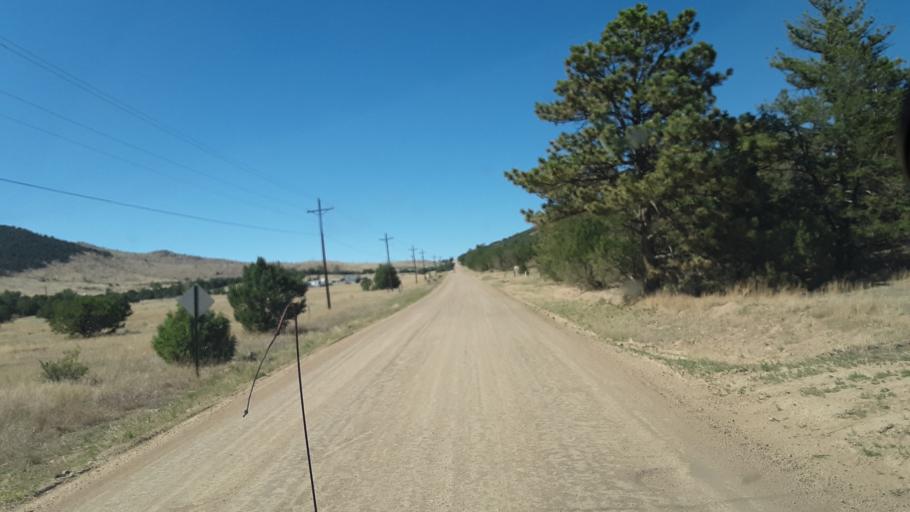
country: US
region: Colorado
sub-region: Custer County
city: Westcliffe
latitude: 38.3121
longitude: -105.4865
